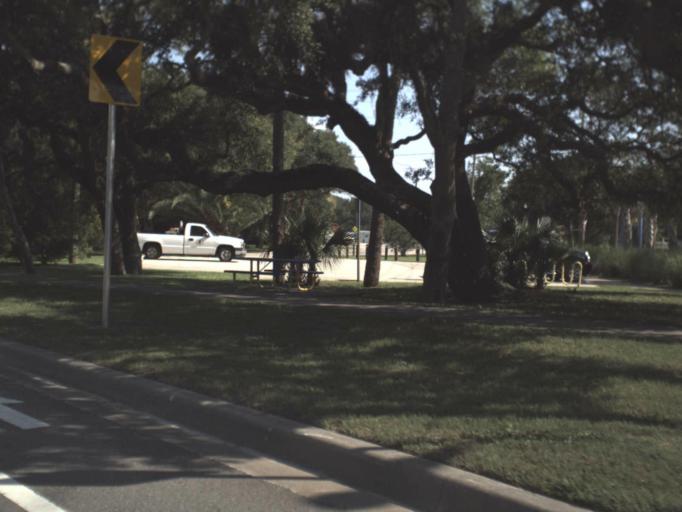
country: US
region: Florida
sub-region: Saint Johns County
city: Saint Augustine
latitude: 29.8810
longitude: -81.2868
